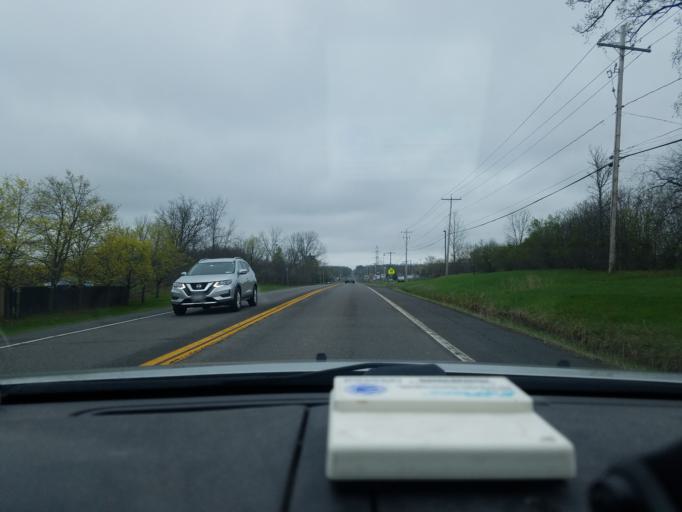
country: US
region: New York
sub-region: Onondaga County
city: North Syracuse
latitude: 43.1595
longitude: -76.0993
